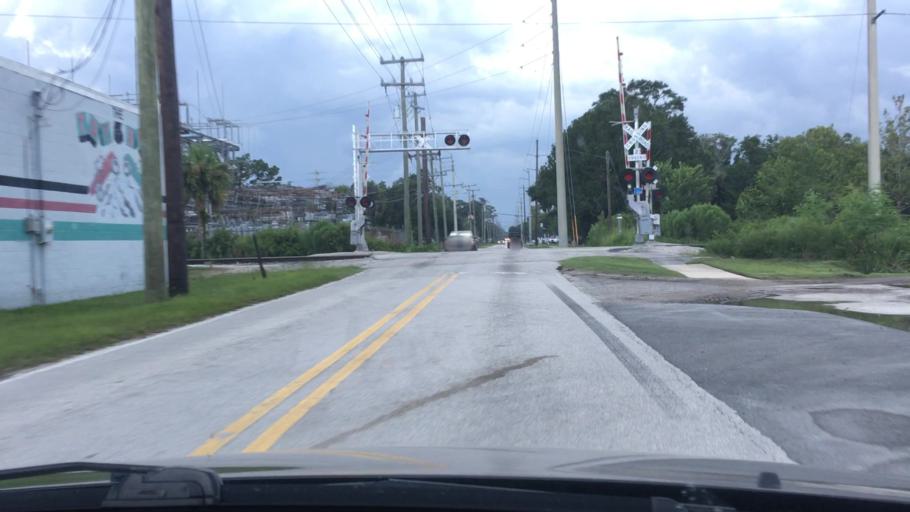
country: US
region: Florida
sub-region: Volusia County
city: Holly Hill
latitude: 29.2482
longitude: -81.0457
